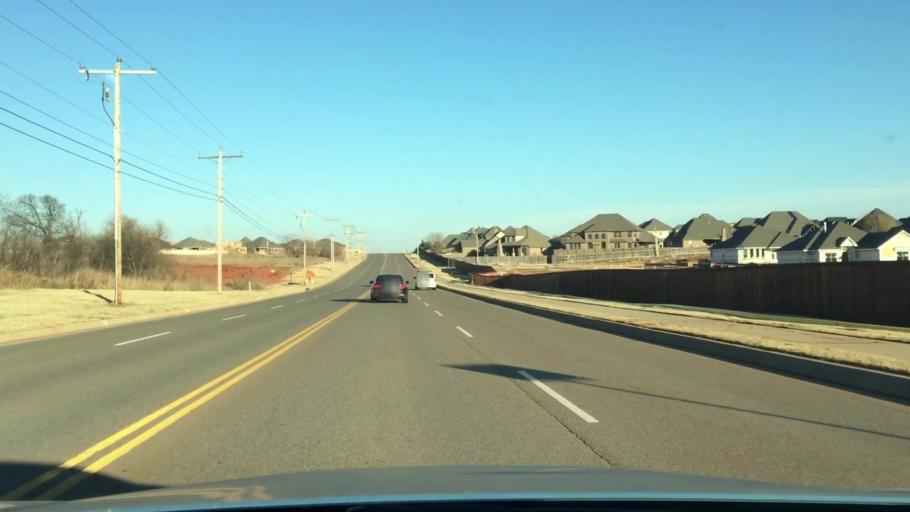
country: US
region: Oklahoma
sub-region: Oklahoma County
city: The Village
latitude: 35.6531
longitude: -97.5786
